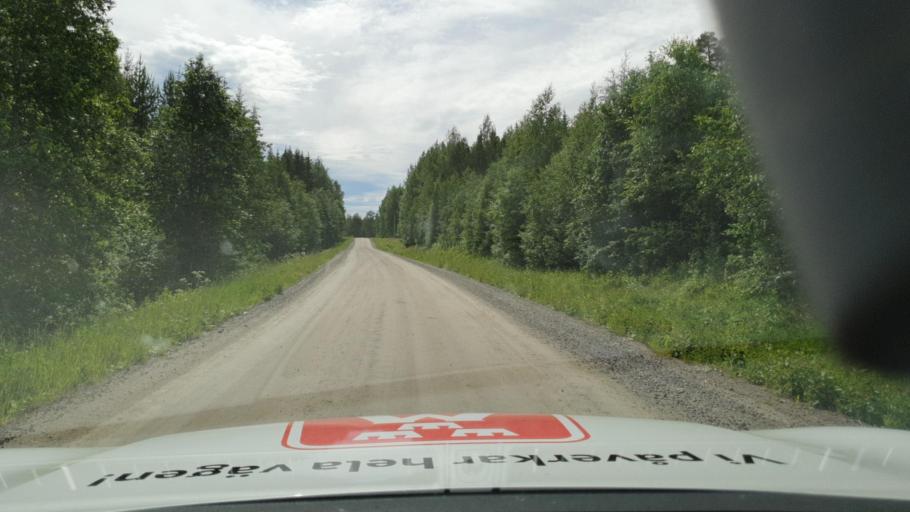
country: SE
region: Vaesterbotten
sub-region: Skelleftea Kommun
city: Burtraesk
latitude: 64.3668
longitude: 20.4113
